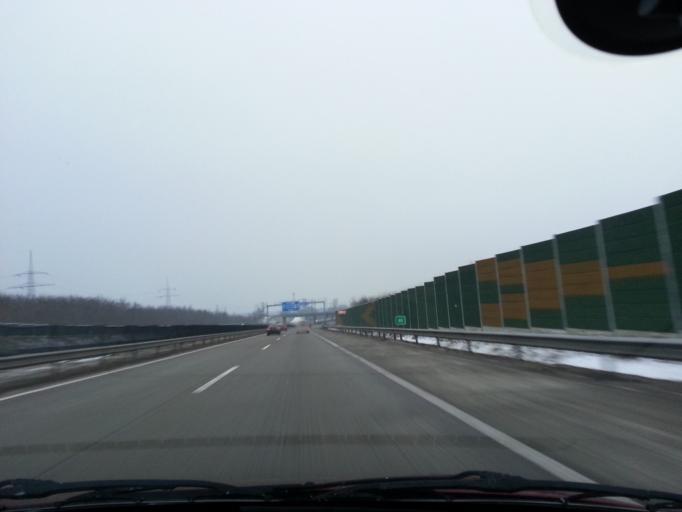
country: HU
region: Pest
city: Ecser
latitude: 47.4455
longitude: 19.3323
